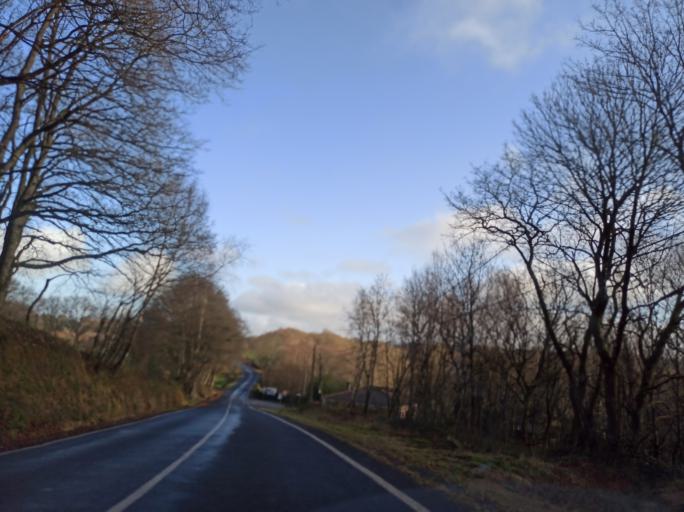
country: ES
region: Galicia
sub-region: Provincia da Coruna
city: Curtis
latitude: 43.0919
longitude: -7.9936
